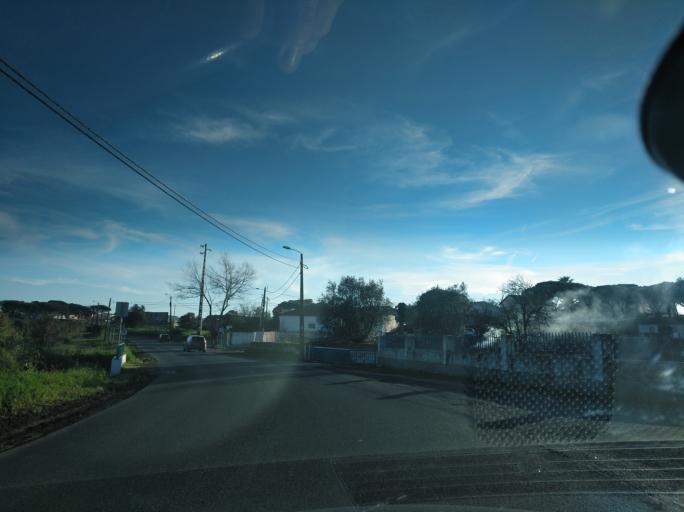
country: PT
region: Lisbon
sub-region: Sintra
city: Sintra
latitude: 38.8310
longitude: -9.3705
